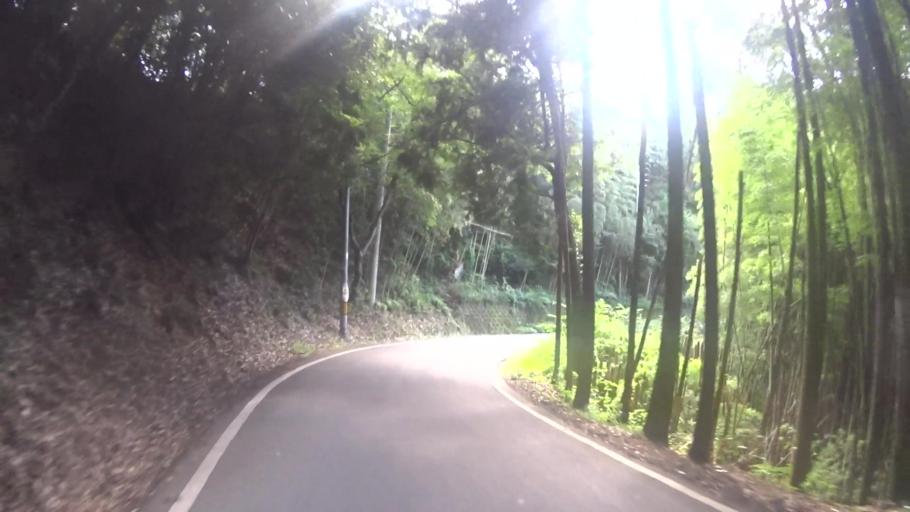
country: JP
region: Nara
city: Nara-shi
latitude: 34.7245
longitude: 135.8871
